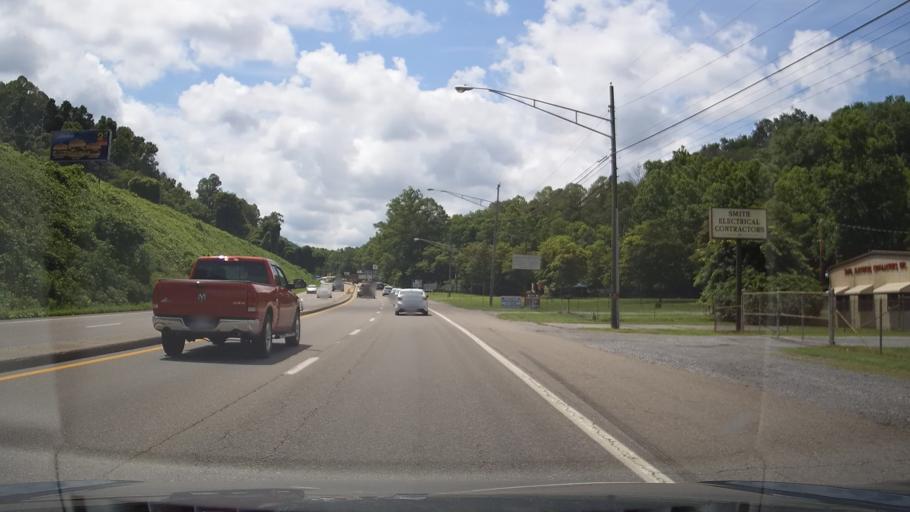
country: US
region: Virginia
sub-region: Scott County
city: Weber City
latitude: 36.6375
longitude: -82.5588
